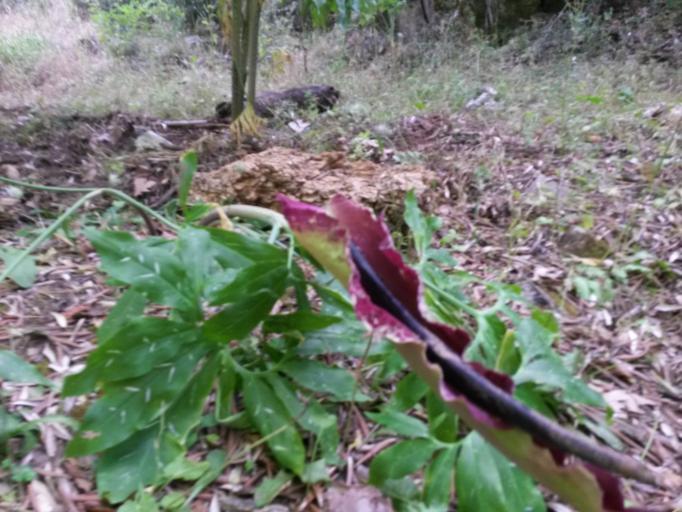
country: GR
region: North Aegean
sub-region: Nomos Lesvou
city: Agiasos
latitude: 39.1124
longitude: 26.3914
